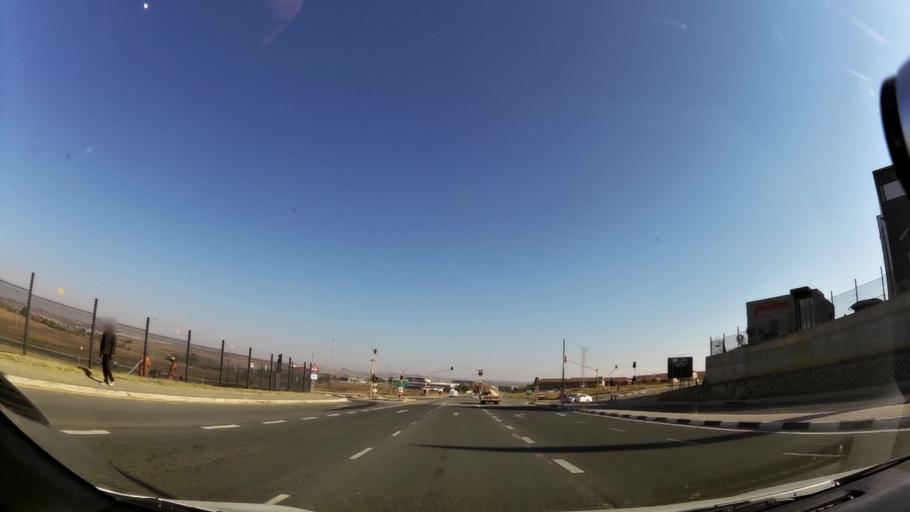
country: ZA
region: Gauteng
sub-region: City of Johannesburg Metropolitan Municipality
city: Midrand
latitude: -25.9215
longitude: 28.1327
